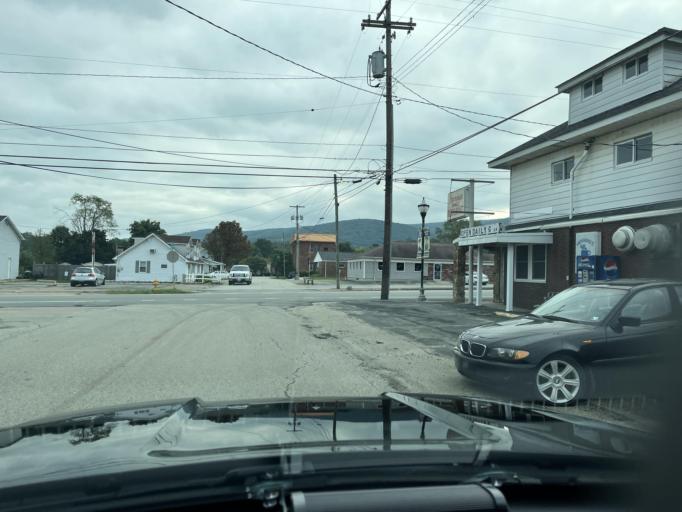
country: US
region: Pennsylvania
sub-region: Fayette County
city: Hopwood
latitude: 39.8735
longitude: -79.6995
